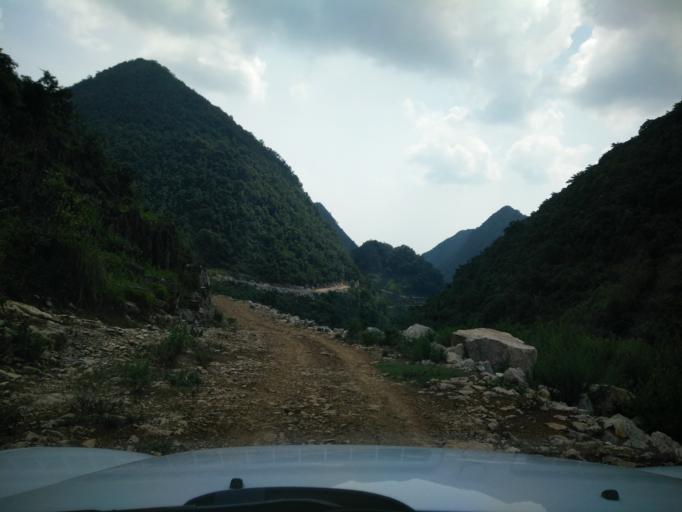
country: CN
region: Guangxi Zhuangzu Zizhiqu
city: Xinzhou
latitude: 25.1335
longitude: 105.6719
